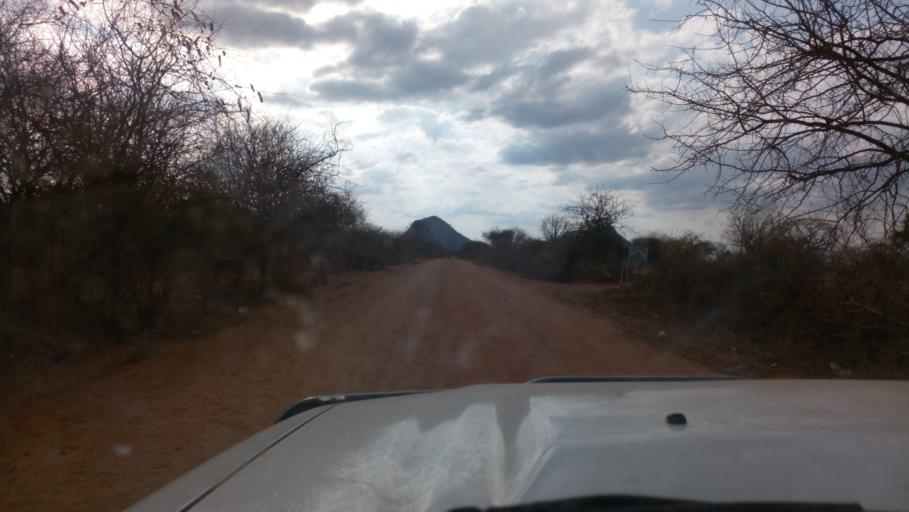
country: KE
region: Kitui
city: Kitui
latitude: -1.7204
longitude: 38.3825
